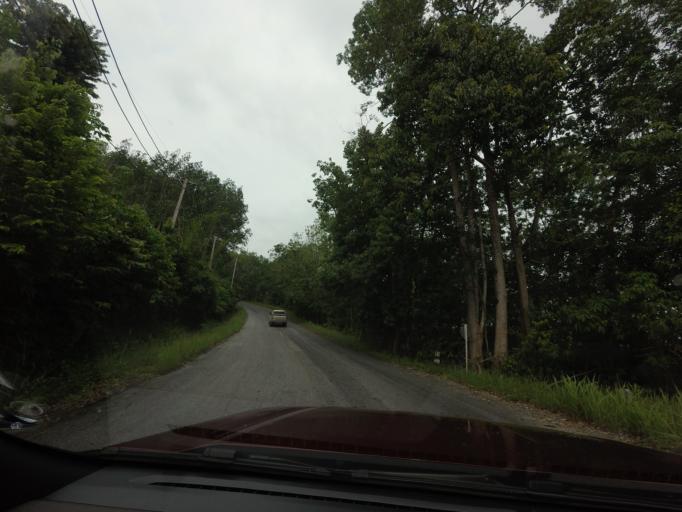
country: TH
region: Yala
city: Than To
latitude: 6.1362
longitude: 101.2915
